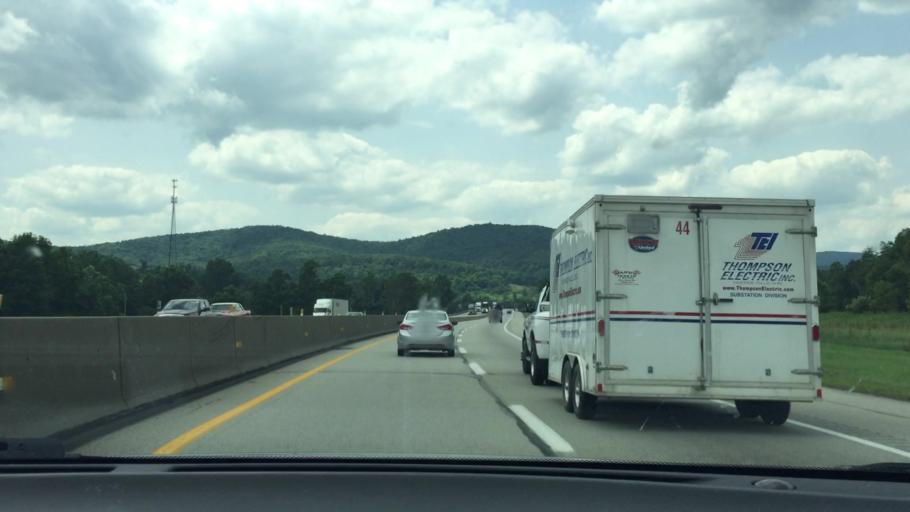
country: US
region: Pennsylvania
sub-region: Somerset County
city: Central City
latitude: 39.9771
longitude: -78.7528
